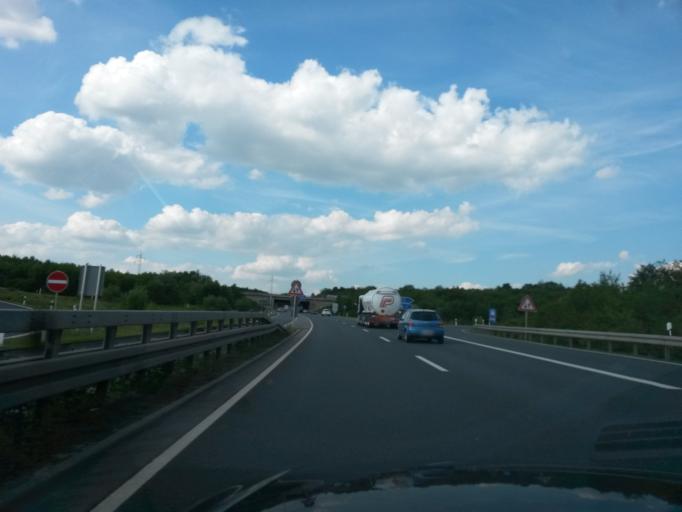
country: DE
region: Bavaria
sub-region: Regierungsbezirk Unterfranken
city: Estenfeld
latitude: 49.8444
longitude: 10.0090
